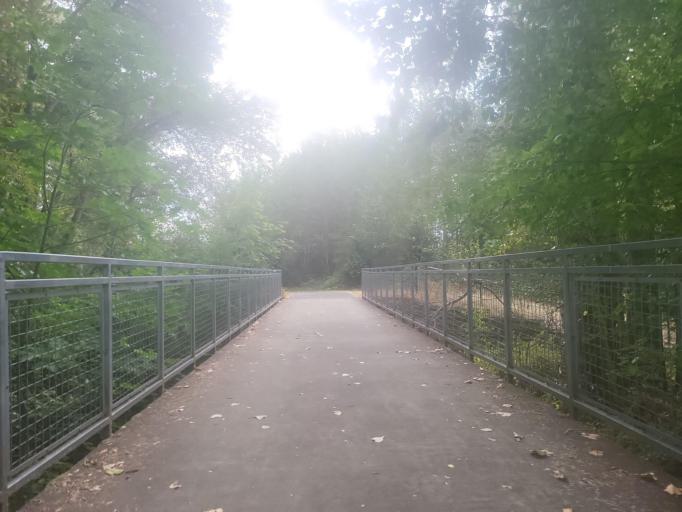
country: US
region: Washington
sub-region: King County
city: Pacific
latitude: 47.2443
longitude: -122.2357
